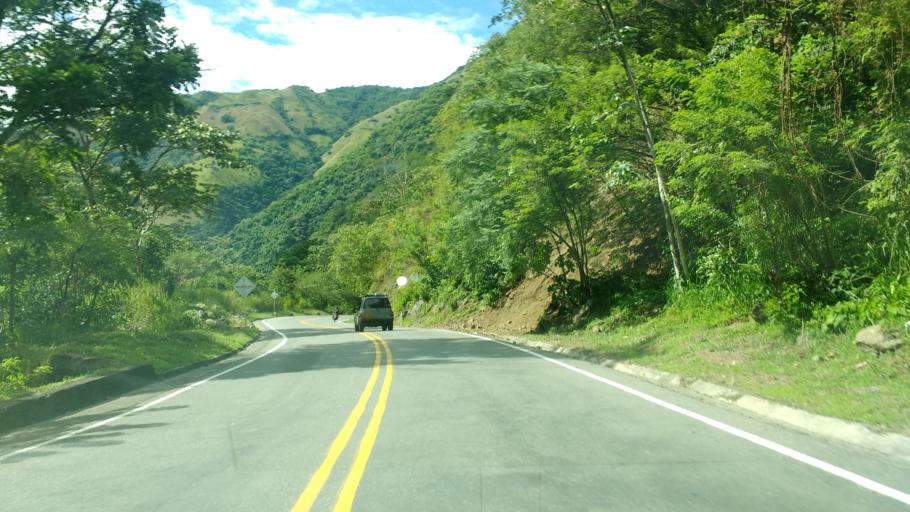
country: CO
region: Antioquia
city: Venecia
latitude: 5.9994
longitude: -75.7886
